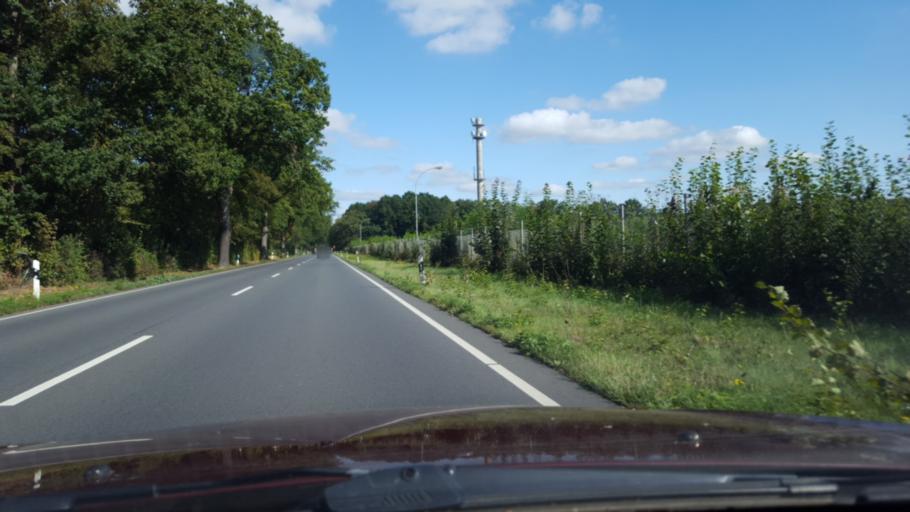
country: DE
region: Lower Saxony
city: Dorverden
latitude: 52.8251
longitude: 9.2048
